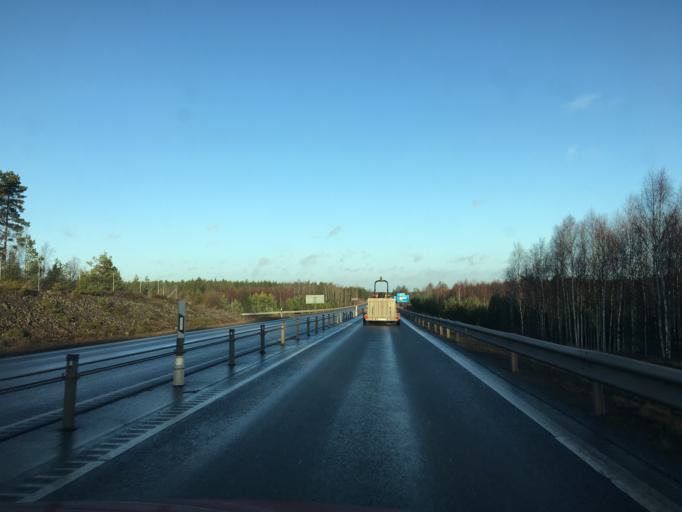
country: SE
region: Kalmar
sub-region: Vasterviks Kommun
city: Vaestervik
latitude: 57.7513
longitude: 16.5577
